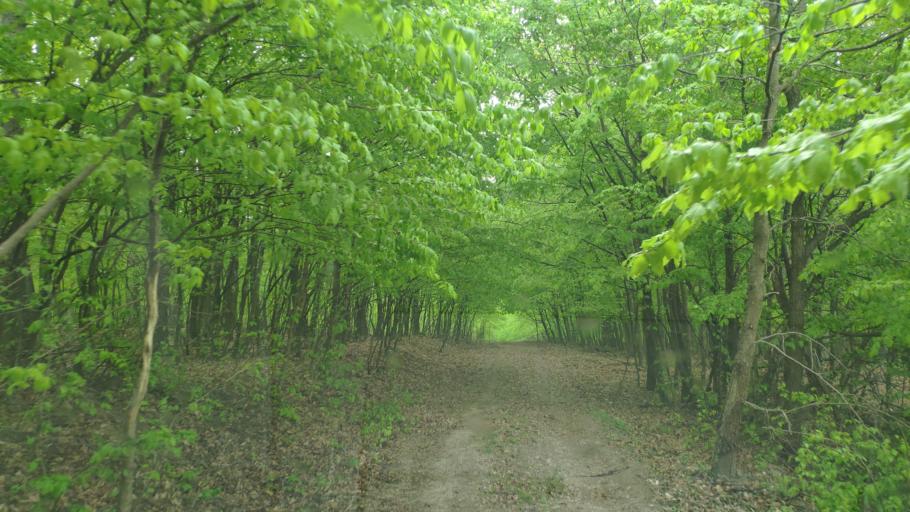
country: SK
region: Kosicky
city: Moldava nad Bodvou
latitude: 48.5441
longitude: 20.9324
